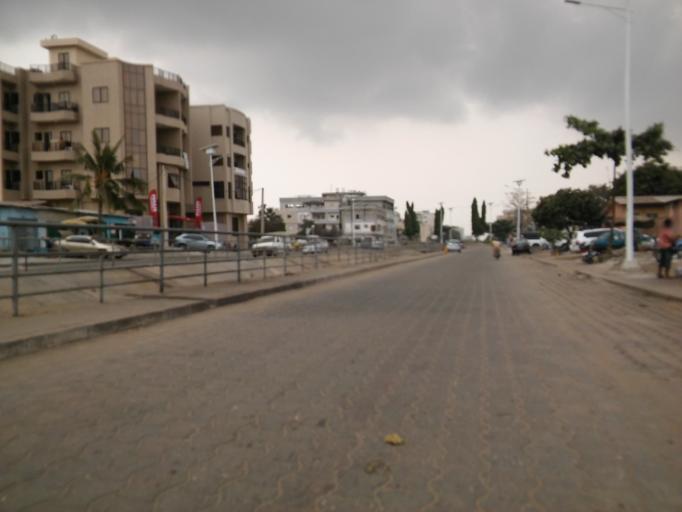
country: BJ
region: Littoral
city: Cotonou
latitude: 6.3804
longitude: 2.4211
